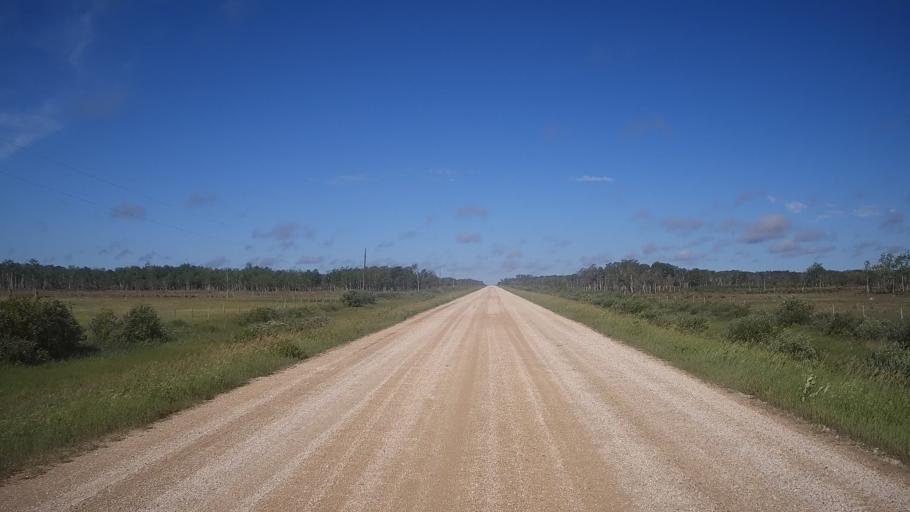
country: CA
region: Manitoba
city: Stonewall
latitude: 50.2411
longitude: -97.7447
